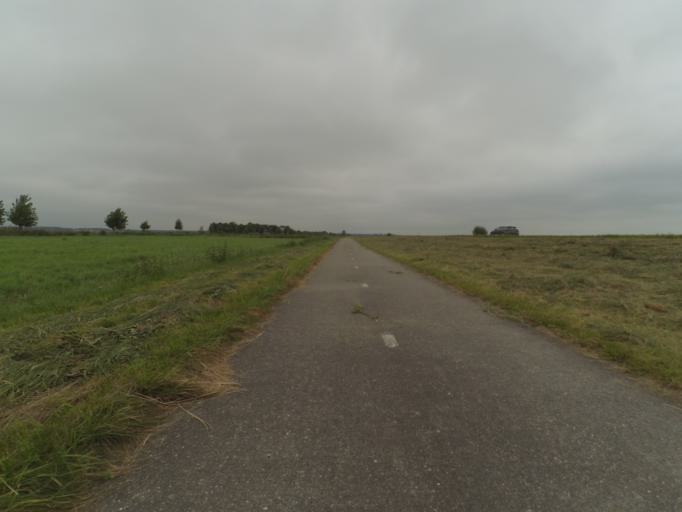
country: NL
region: Flevoland
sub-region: Gemeente Lelystad
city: Lelystad
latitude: 52.4302
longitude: 5.5257
